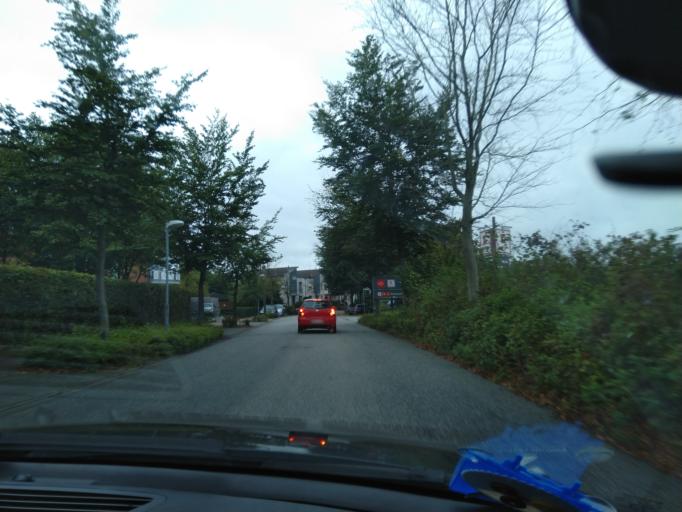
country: DE
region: Lower Saxony
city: Nordhorn
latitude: 52.4239
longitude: 7.0781
